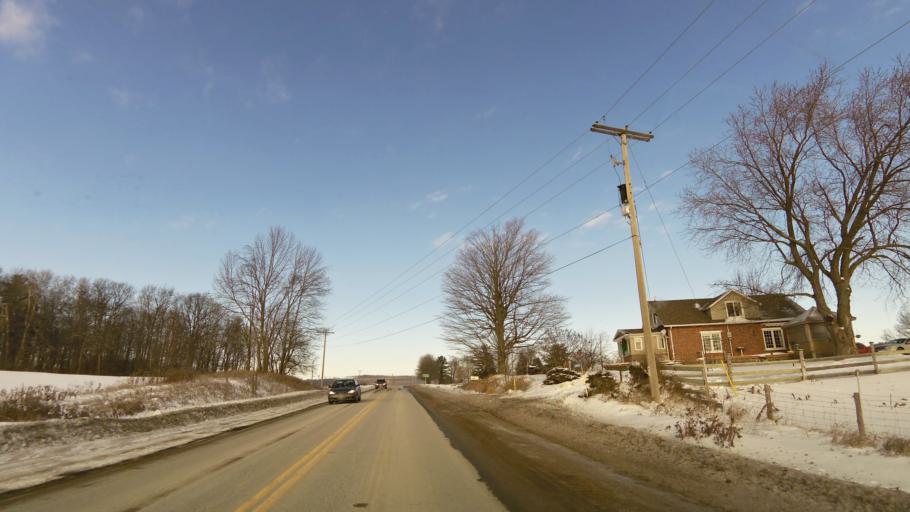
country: CA
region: Ontario
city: Quinte West
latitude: 44.1431
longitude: -77.7911
